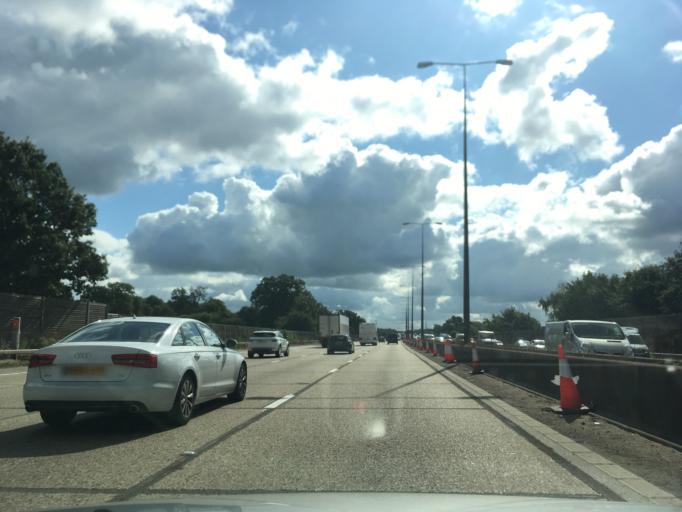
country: GB
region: England
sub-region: Surrey
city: Addlestone
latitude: 51.3613
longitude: -0.4982
